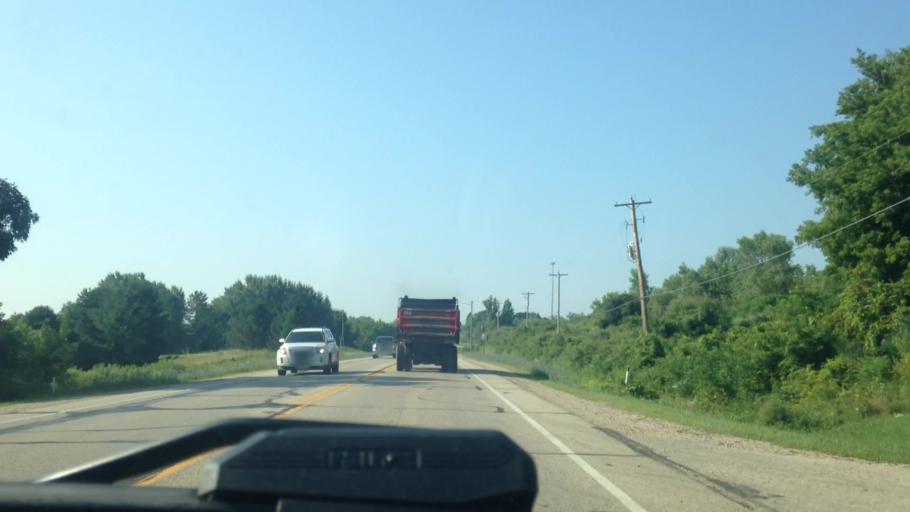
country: US
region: Wisconsin
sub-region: Waukesha County
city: Merton
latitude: 43.1708
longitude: -88.2625
